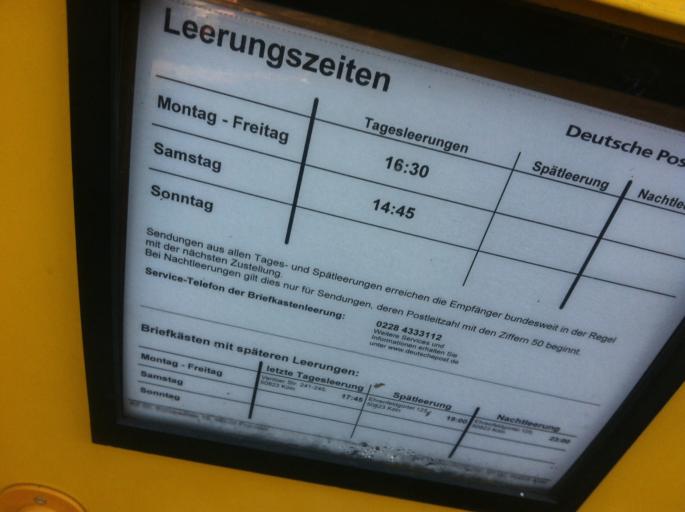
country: DE
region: North Rhine-Westphalia
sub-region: Regierungsbezirk Koln
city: Neuehrenfeld
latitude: 50.9406
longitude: 6.9103
